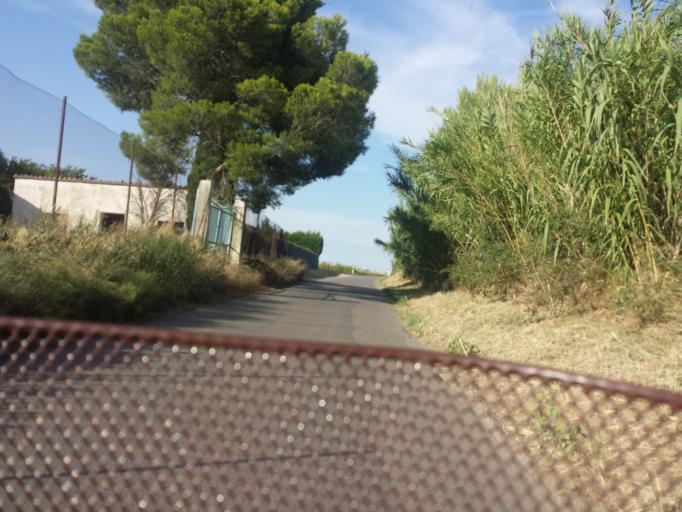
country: ES
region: Aragon
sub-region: Provincia de Zaragoza
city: Zaragoza
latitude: 41.6986
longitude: -0.8586
